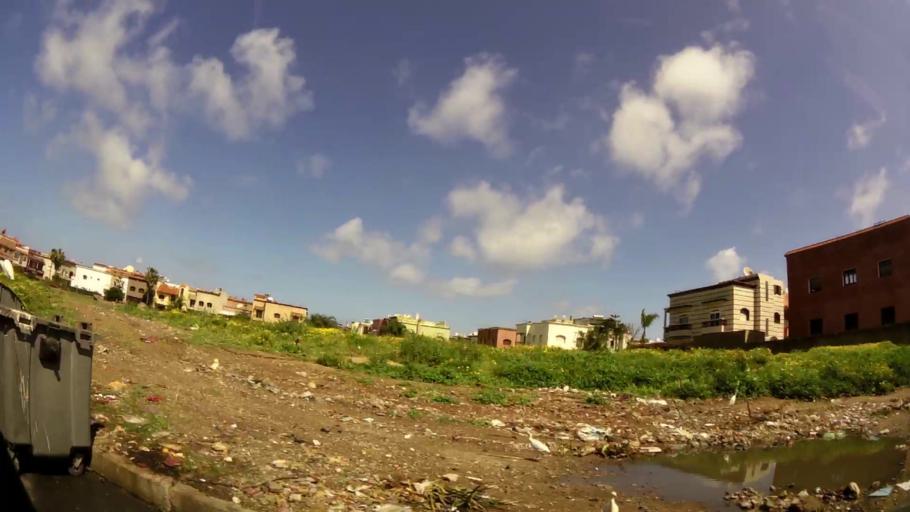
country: MA
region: Grand Casablanca
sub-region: Mediouna
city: Tit Mellil
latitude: 33.6165
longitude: -7.5253
